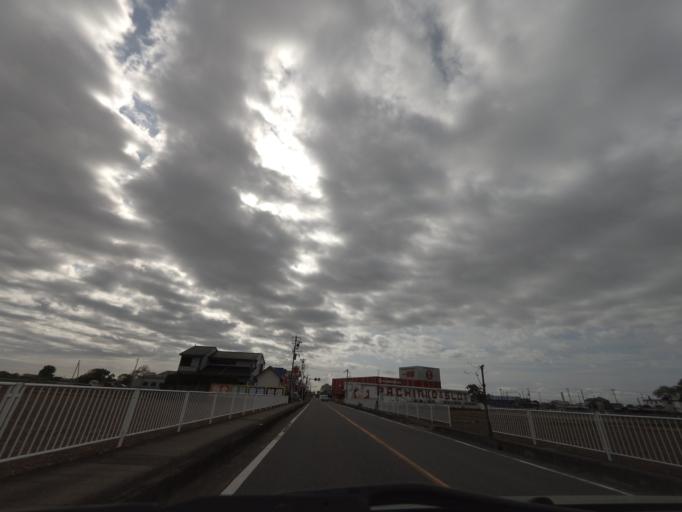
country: JP
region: Saitama
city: Kamifukuoka
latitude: 35.8848
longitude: 139.5435
